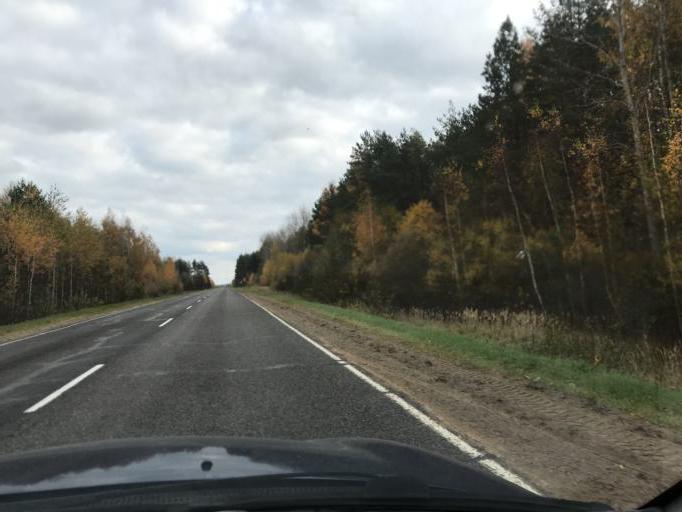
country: BY
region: Grodnenskaya
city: Lida
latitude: 53.7431
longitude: 25.3364
